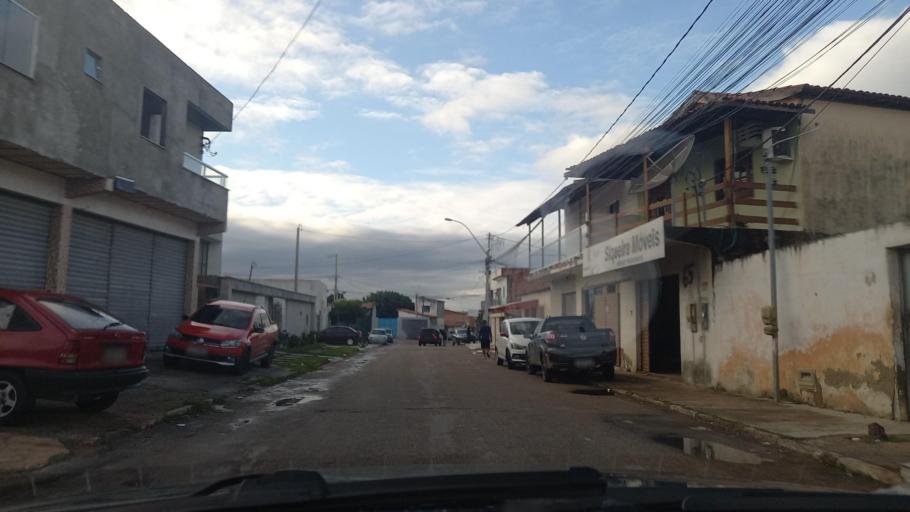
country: BR
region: Bahia
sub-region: Paulo Afonso
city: Paulo Afonso
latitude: -9.3881
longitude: -38.2322
